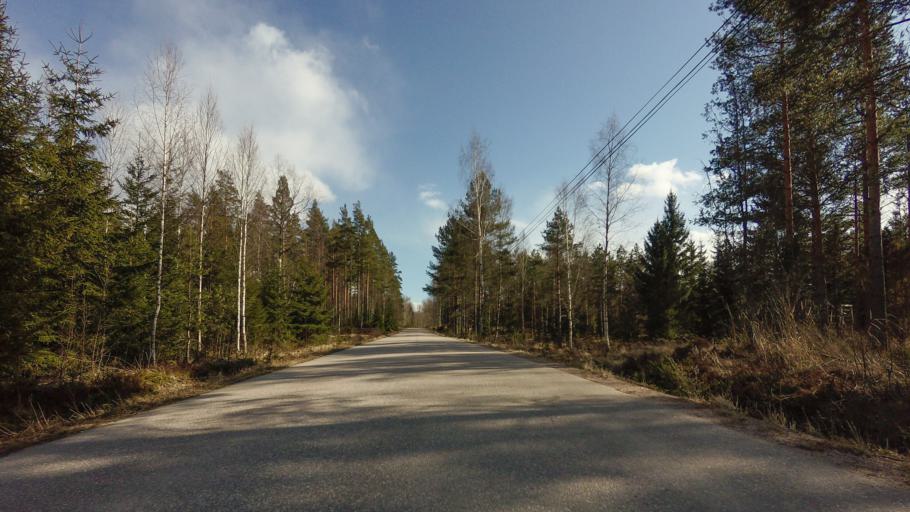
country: FI
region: Varsinais-Suomi
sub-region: Salo
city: Suomusjaervi
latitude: 60.3264
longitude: 23.6487
